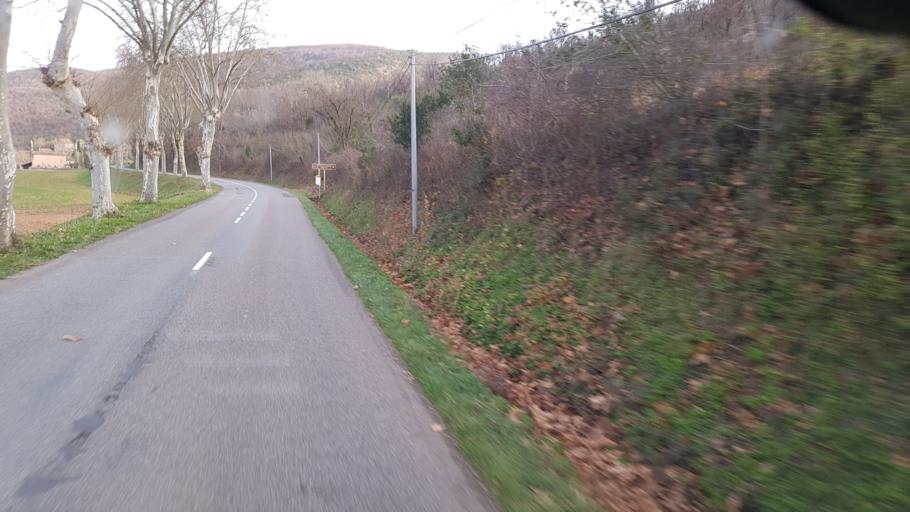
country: FR
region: Midi-Pyrenees
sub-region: Departement du Tarn-et-Garonne
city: Montricoux
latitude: 44.0054
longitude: 1.6821
